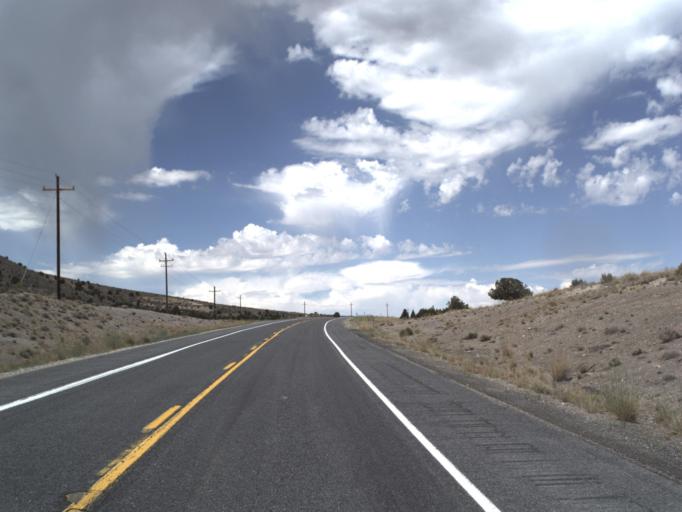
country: US
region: Utah
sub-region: Utah County
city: Eagle Mountain
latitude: 40.0734
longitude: -112.3607
